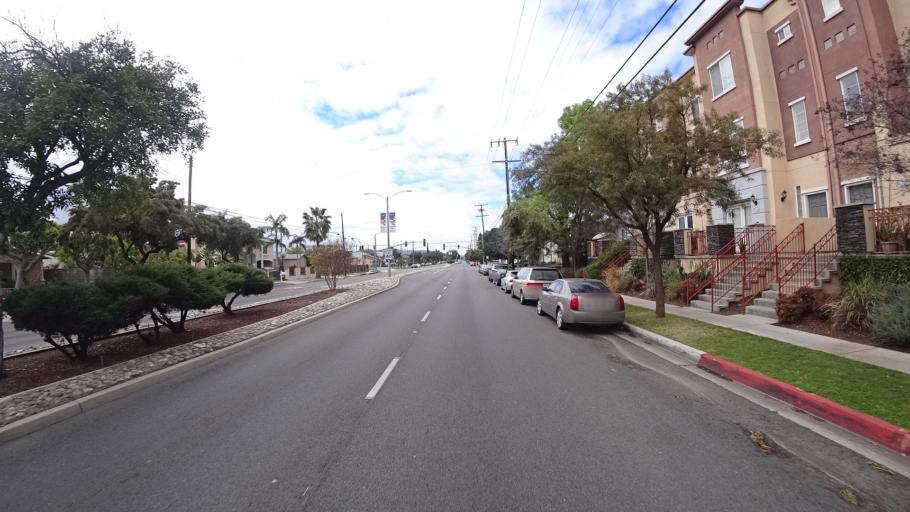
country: US
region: California
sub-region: Los Angeles County
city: Baldwin Park
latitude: 34.0750
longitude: -117.9742
